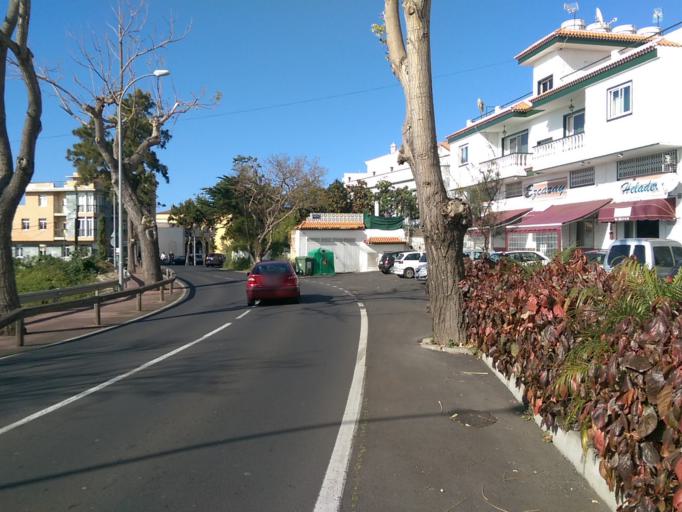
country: ES
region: Canary Islands
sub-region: Provincia de Santa Cruz de Tenerife
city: La Victoria de Acentejo
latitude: 28.4451
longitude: -16.4589
